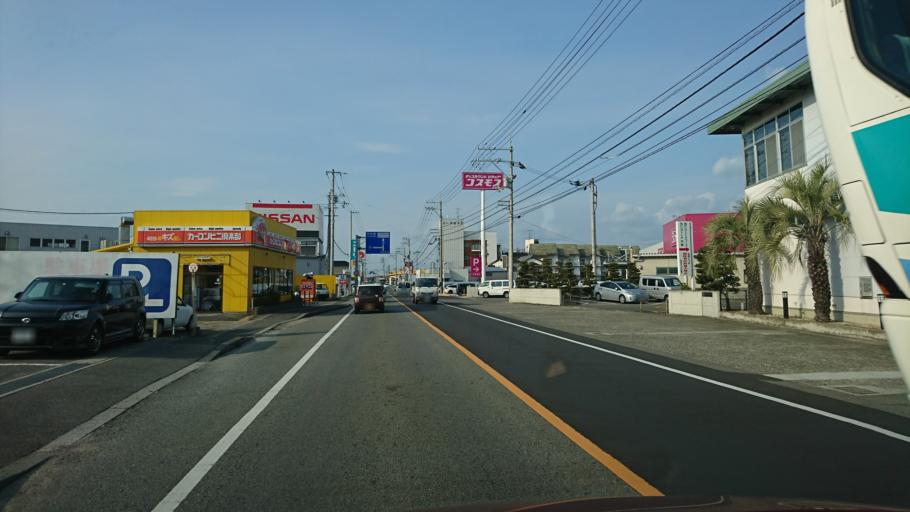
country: JP
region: Ehime
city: Saijo
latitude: 34.0351
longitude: 133.0342
